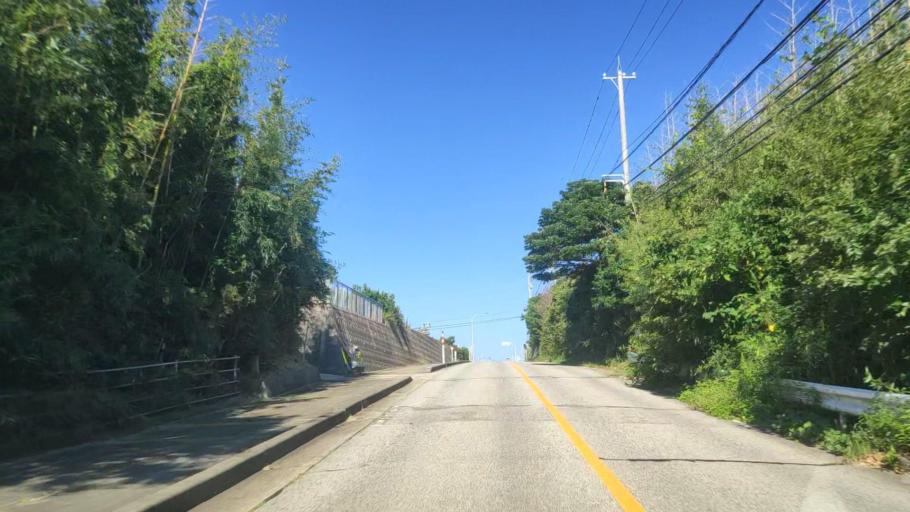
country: JP
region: Ishikawa
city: Hakui
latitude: 37.0518
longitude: 136.7335
